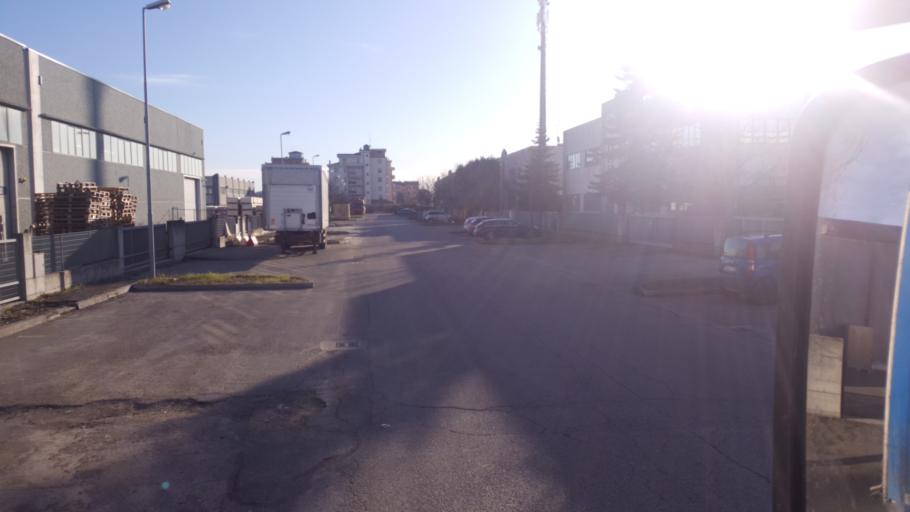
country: IT
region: Emilia-Romagna
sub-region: Provincia di Reggio Emilia
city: Rubiera
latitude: 44.6577
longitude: 10.7762
